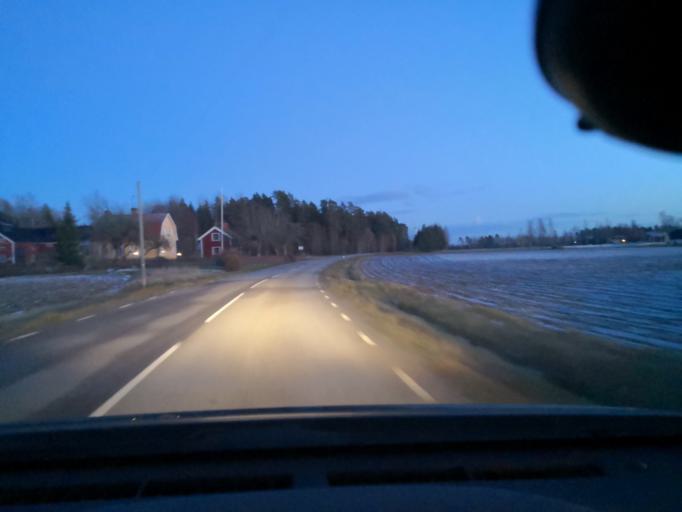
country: SE
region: Vaestmanland
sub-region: Sala Kommun
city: Sala
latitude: 59.8751
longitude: 16.7002
